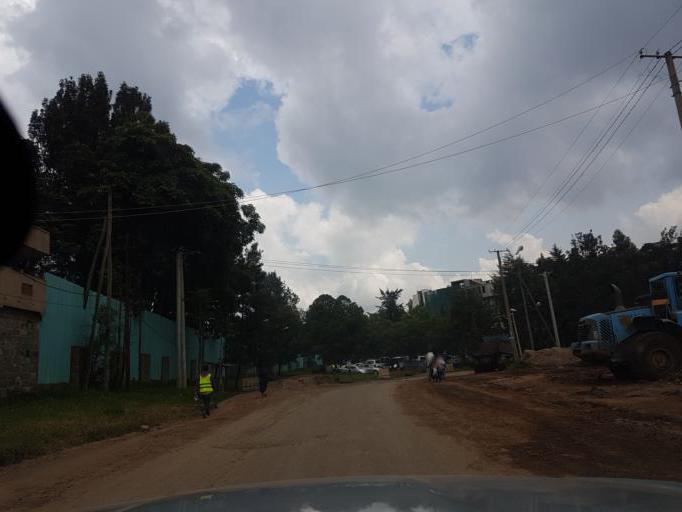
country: ET
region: Adis Abeba
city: Addis Ababa
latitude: 9.0265
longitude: 38.7665
